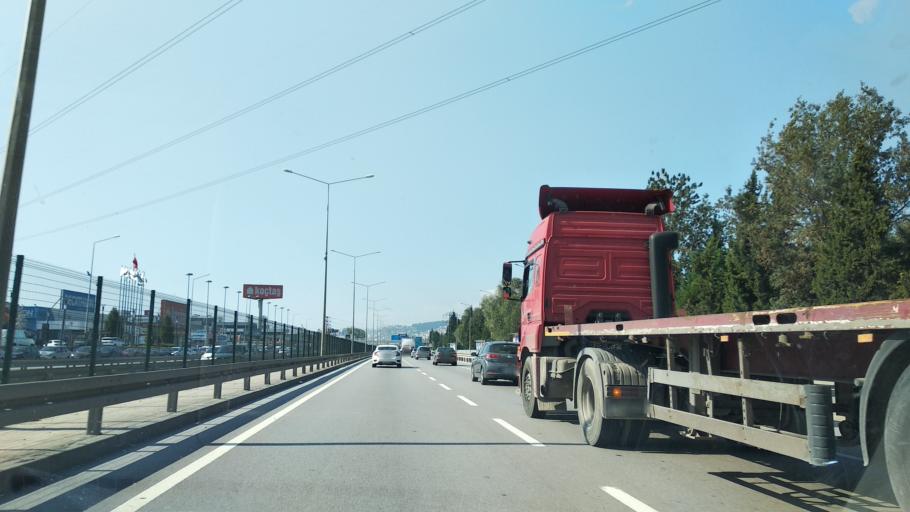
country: TR
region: Kocaeli
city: Kullar
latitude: 40.7596
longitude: 29.9804
